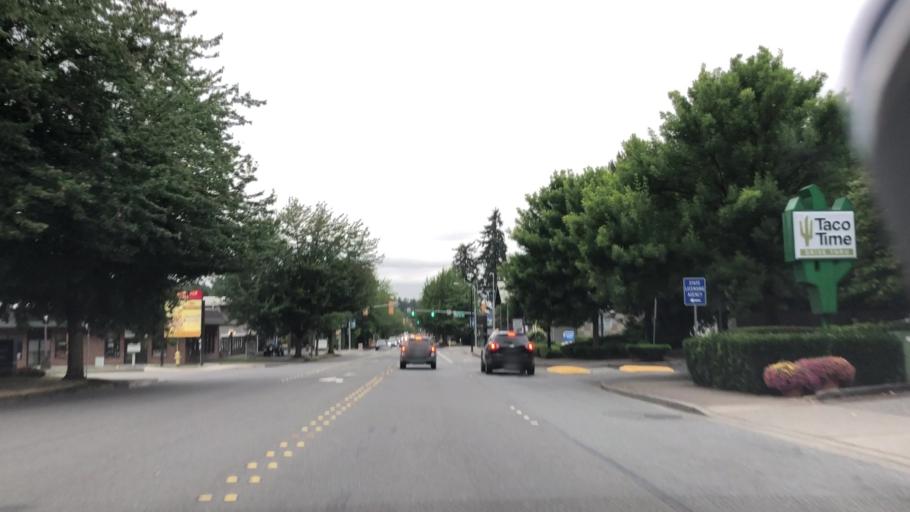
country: US
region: Washington
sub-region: King County
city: Woodinville
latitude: 47.7545
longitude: -122.1535
